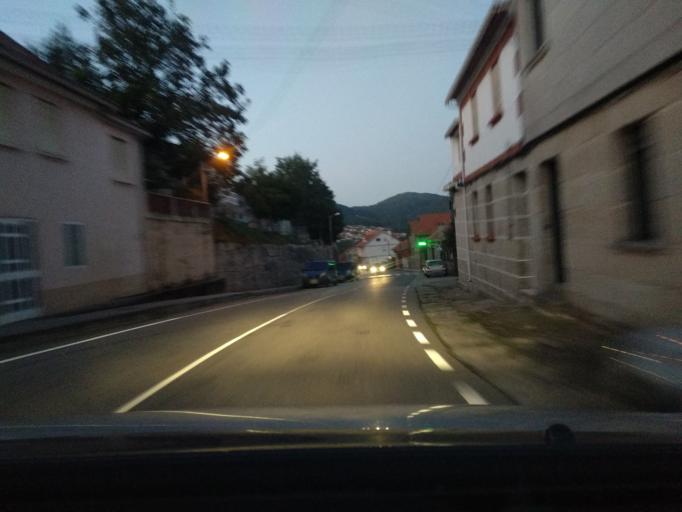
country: ES
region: Galicia
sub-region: Provincia de Pontevedra
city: Moana
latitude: 42.2831
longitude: -8.7435
